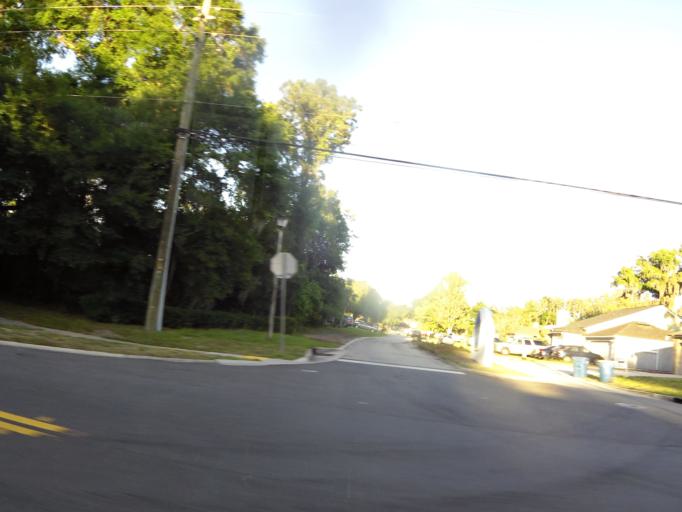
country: US
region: Florida
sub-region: Duval County
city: Atlantic Beach
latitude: 30.3651
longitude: -81.5155
